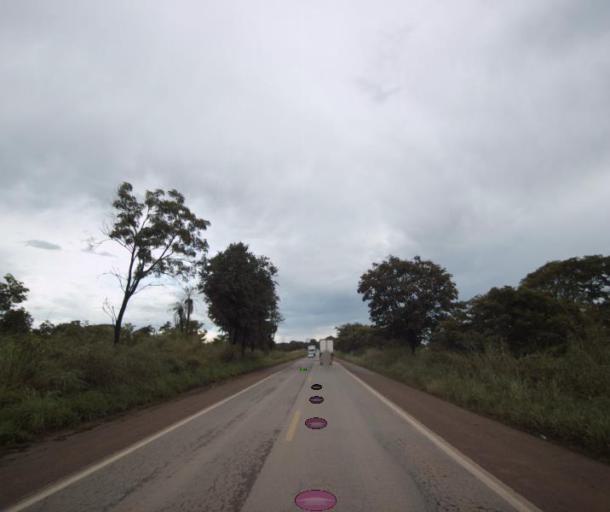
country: BR
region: Goias
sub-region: Porangatu
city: Porangatu
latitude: -13.7004
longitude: -49.0216
